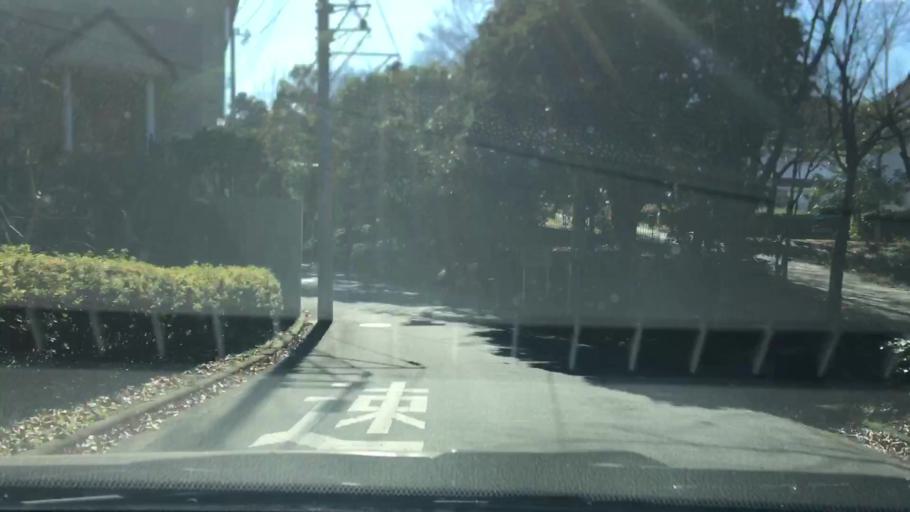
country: JP
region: Tokyo
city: Chofugaoka
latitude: 35.5482
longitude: 139.5668
